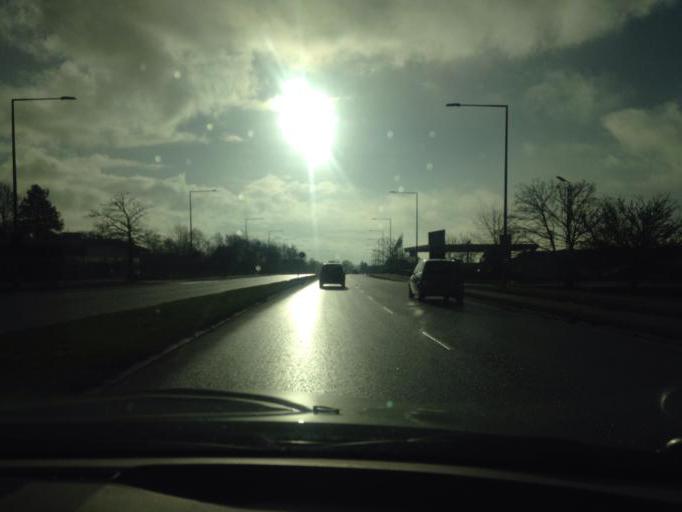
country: DK
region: South Denmark
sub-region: Kolding Kommune
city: Kolding
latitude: 55.5022
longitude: 9.4582
